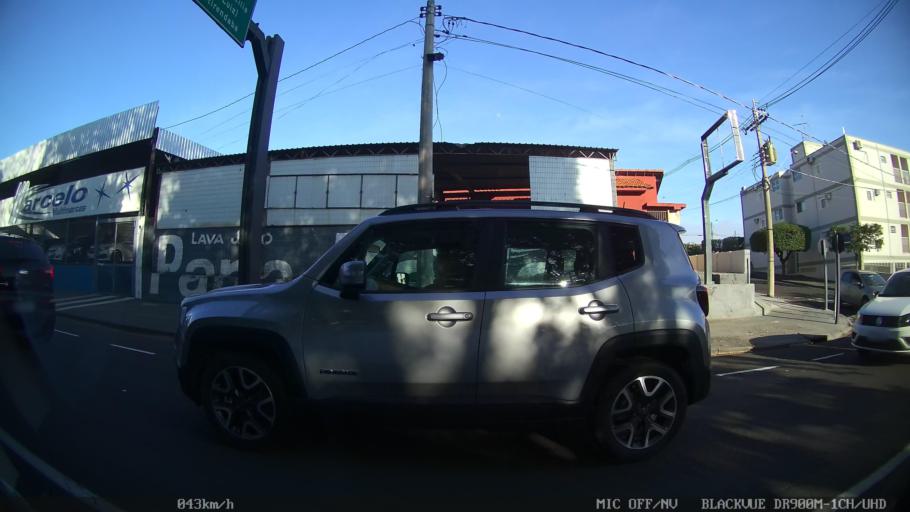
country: BR
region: Sao Paulo
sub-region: Sao Jose Do Rio Preto
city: Sao Jose do Rio Preto
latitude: -20.8158
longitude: -49.3667
